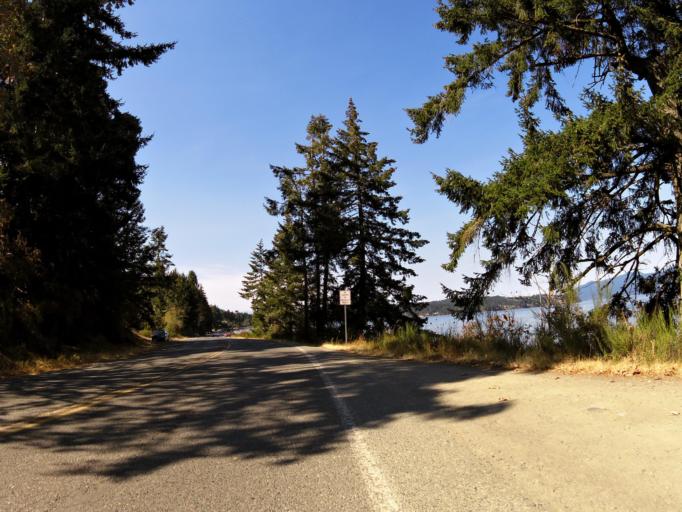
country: CA
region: British Columbia
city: North Saanich
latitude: 48.6324
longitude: -123.5305
